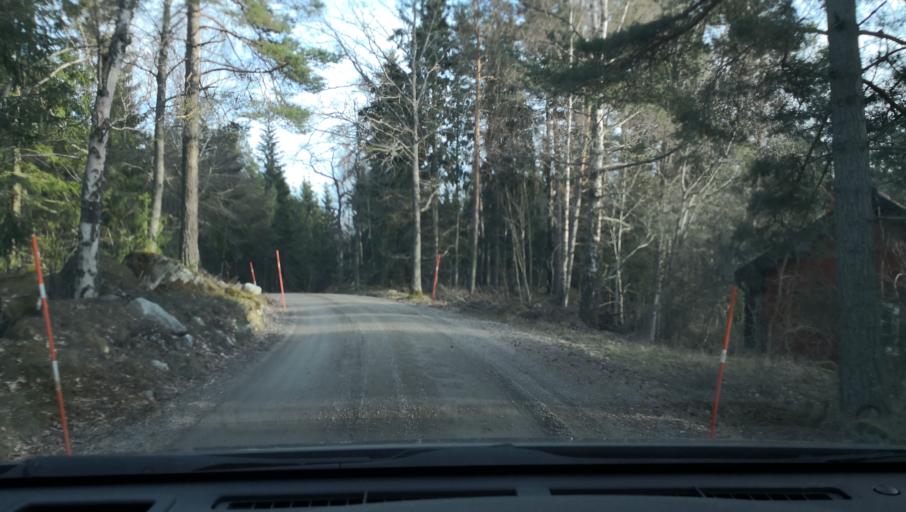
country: SE
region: Uppsala
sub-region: Enkopings Kommun
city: Dalby
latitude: 59.4810
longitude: 17.2530
